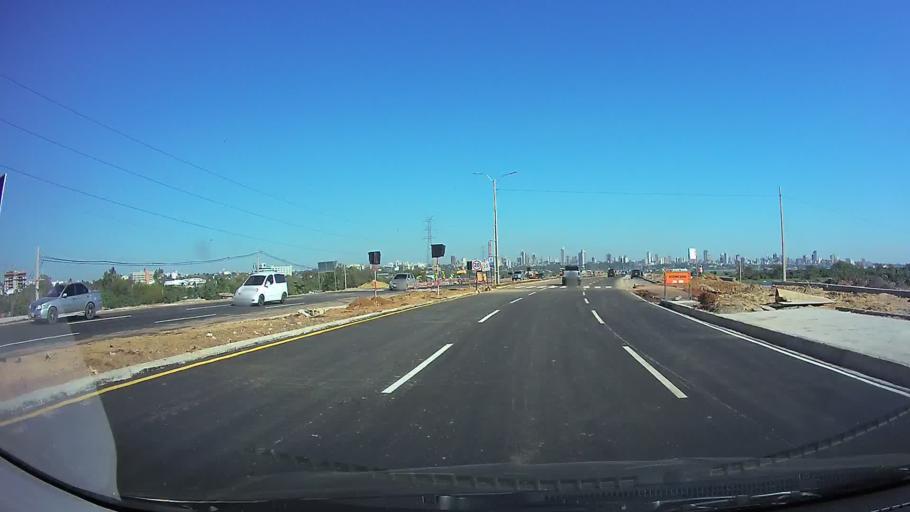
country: PY
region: Asuncion
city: Asuncion
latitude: -25.2629
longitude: -57.6072
